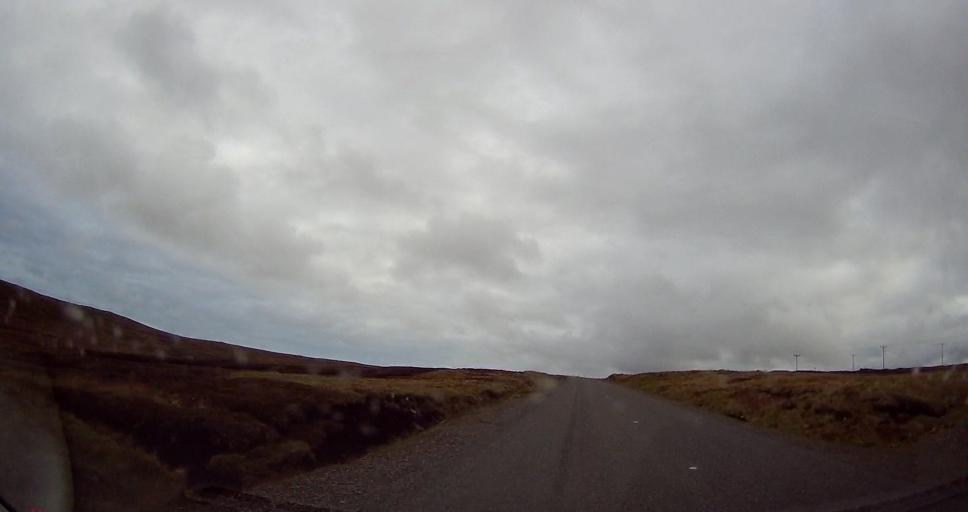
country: GB
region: Scotland
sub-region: Shetland Islands
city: Shetland
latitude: 60.6219
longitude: -1.0743
